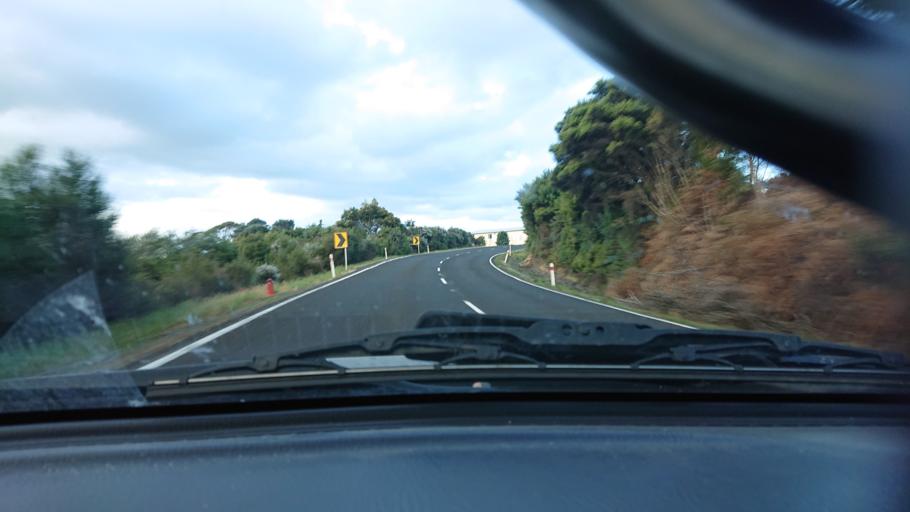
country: NZ
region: Auckland
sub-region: Auckland
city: Parakai
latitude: -36.4759
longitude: 174.4477
